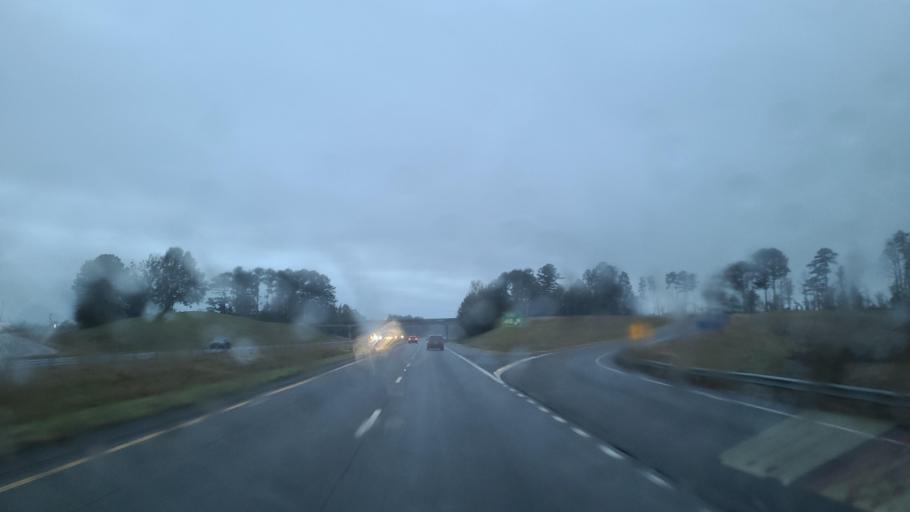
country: US
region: Alabama
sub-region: Greene County
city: Eutaw
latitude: 32.9187
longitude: -87.8690
